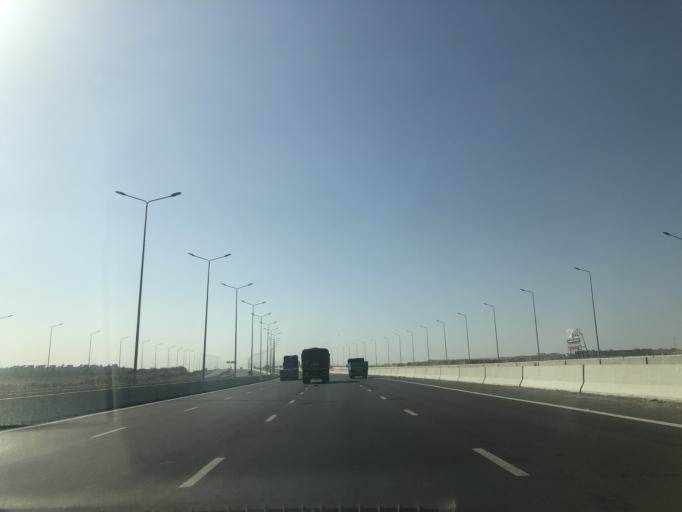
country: EG
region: Al Jizah
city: Madinat Sittah Uktubar
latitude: 29.9670
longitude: 30.8843
